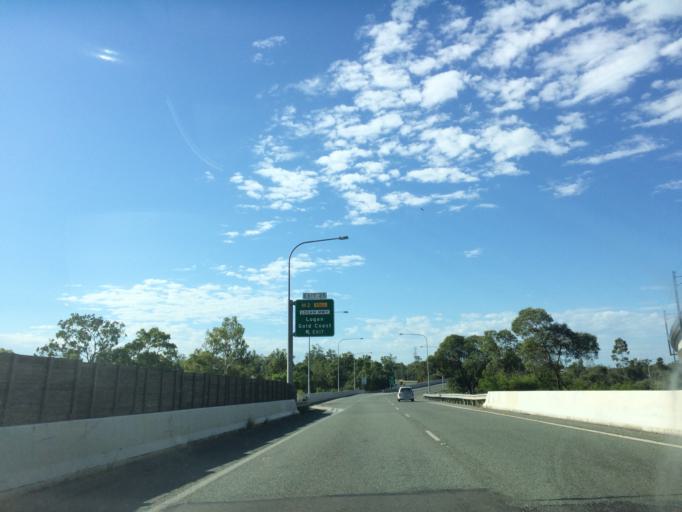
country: AU
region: Queensland
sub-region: Brisbane
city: Forest Lake
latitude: -27.6221
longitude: 152.9427
